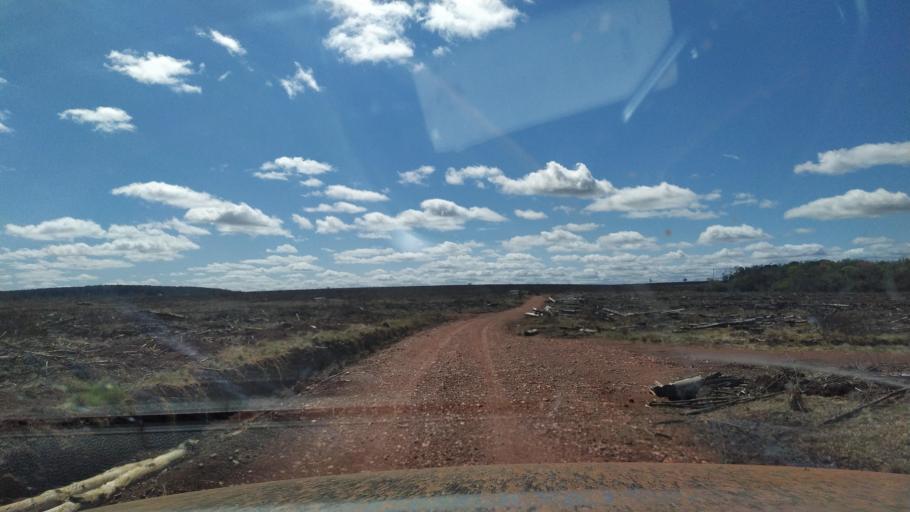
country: AR
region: Corrientes
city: Gobernador Ingeniero Valentin Virasoro
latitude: -28.2942
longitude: -56.0530
